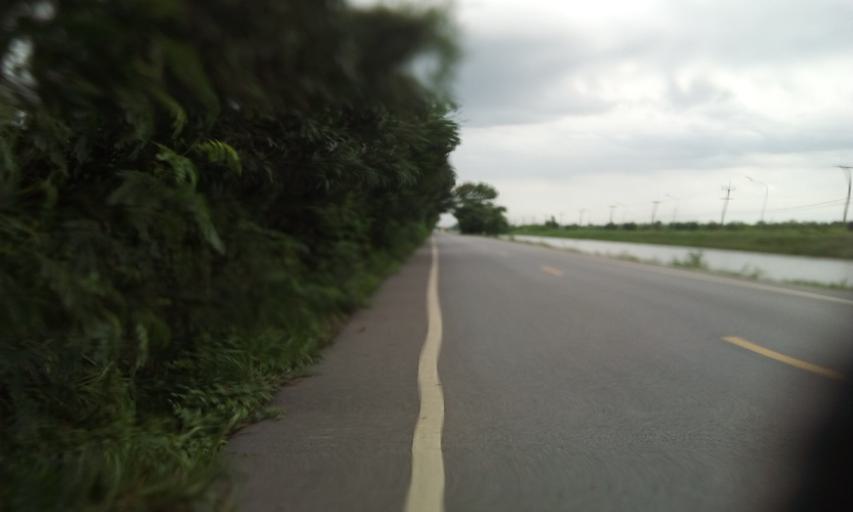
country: TH
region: Pathum Thani
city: Nong Suea
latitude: 14.0725
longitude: 100.8467
